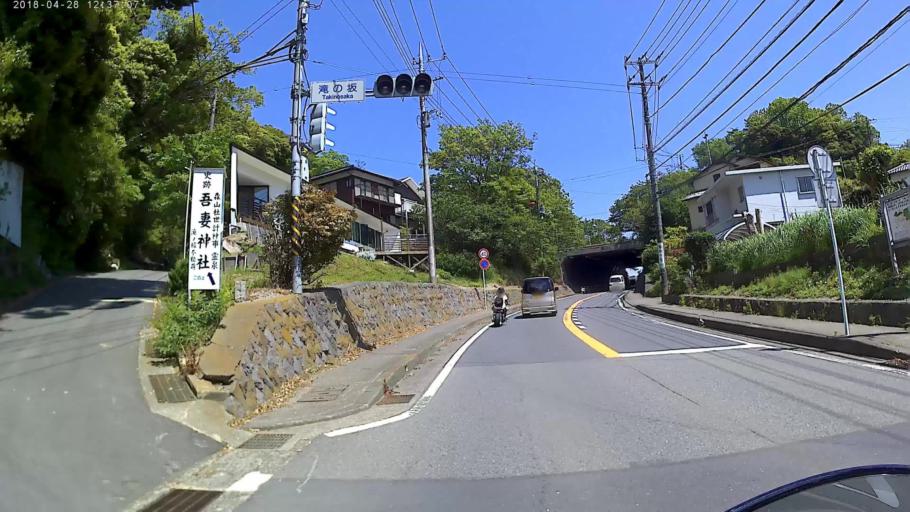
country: JP
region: Kanagawa
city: Hayama
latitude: 35.2654
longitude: 139.5972
